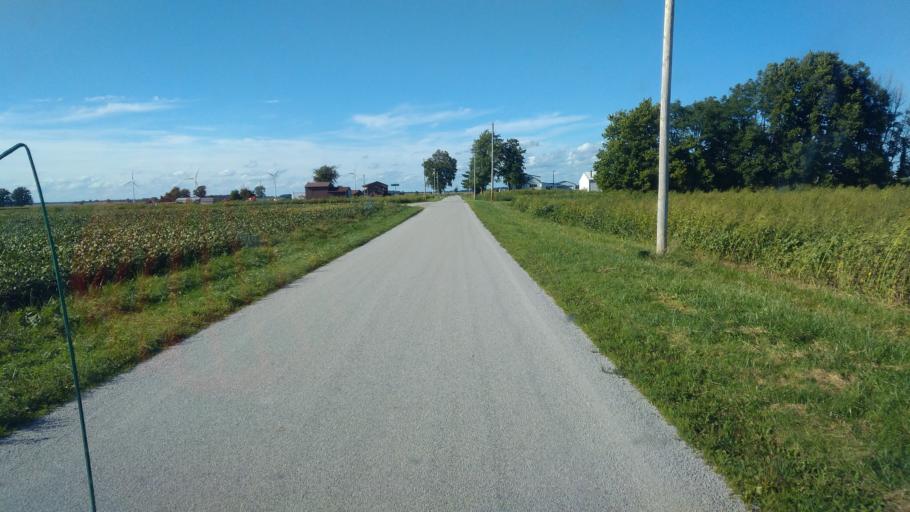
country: US
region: Ohio
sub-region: Hardin County
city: Ada
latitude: 40.7681
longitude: -83.7095
